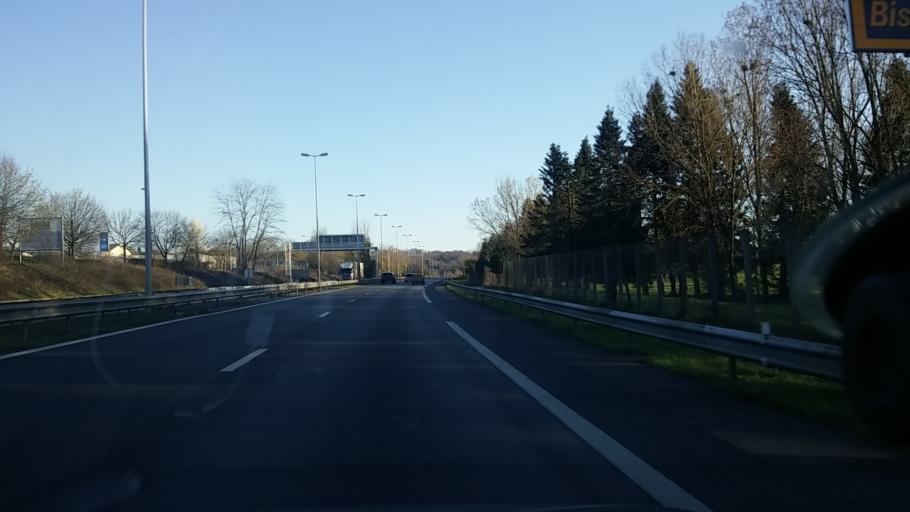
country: FR
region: Limousin
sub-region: Departement de la Haute-Vienne
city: Condat-sur-Vienne
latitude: 45.8137
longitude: 1.2970
